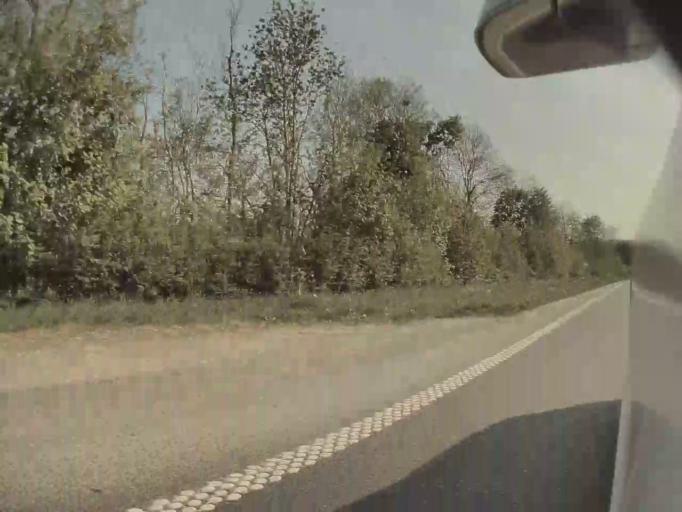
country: BE
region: Wallonia
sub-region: Province de Namur
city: Ciney
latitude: 50.3018
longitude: 5.1207
